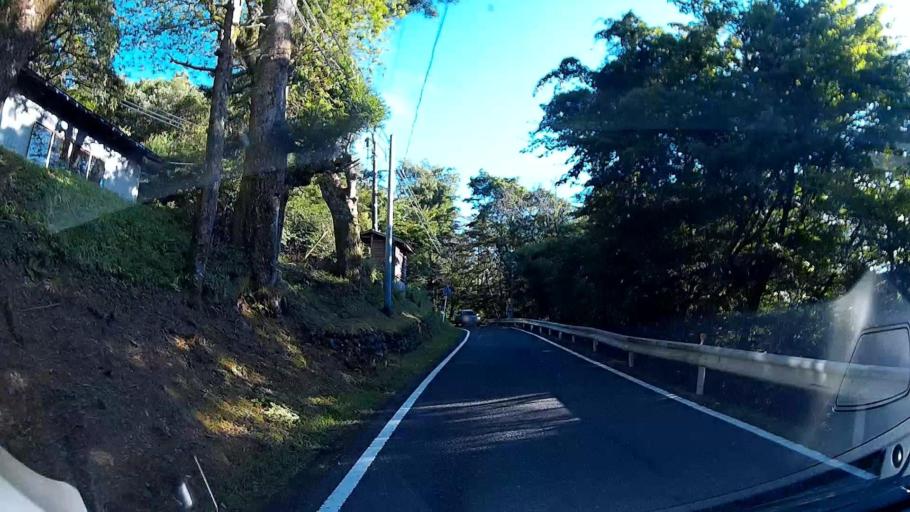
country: JP
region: Shizuoka
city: Shizuoka-shi
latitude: 35.1974
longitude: 138.2521
